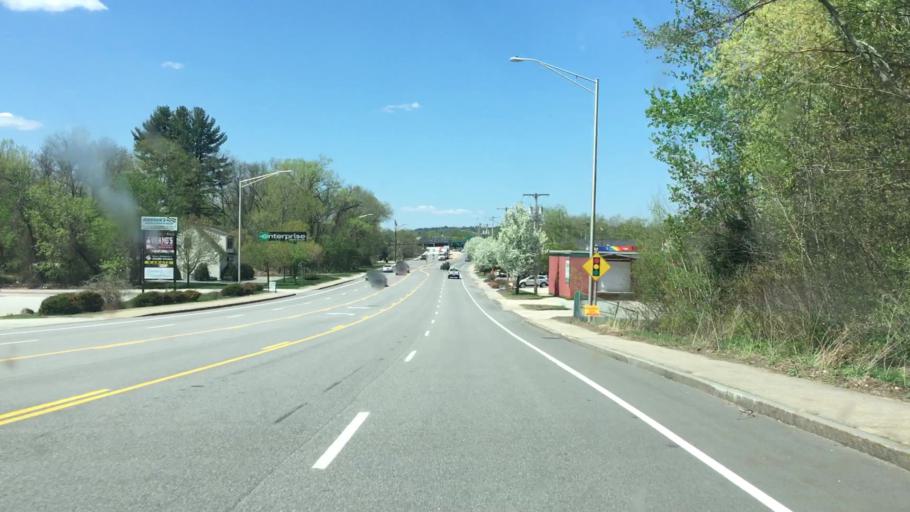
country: US
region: New Hampshire
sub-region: Merrimack County
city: Concord
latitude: 43.1922
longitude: -71.5174
